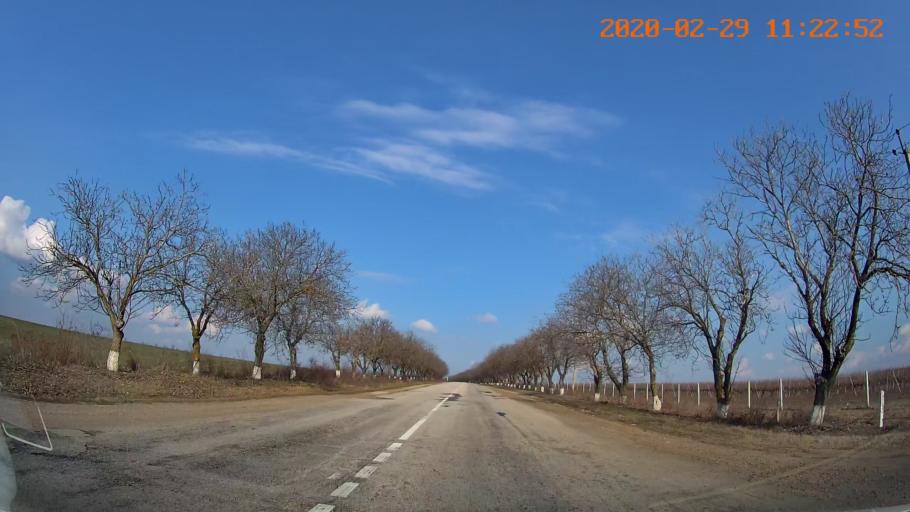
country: MD
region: Telenesti
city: Cocieri
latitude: 47.3997
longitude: 29.1609
